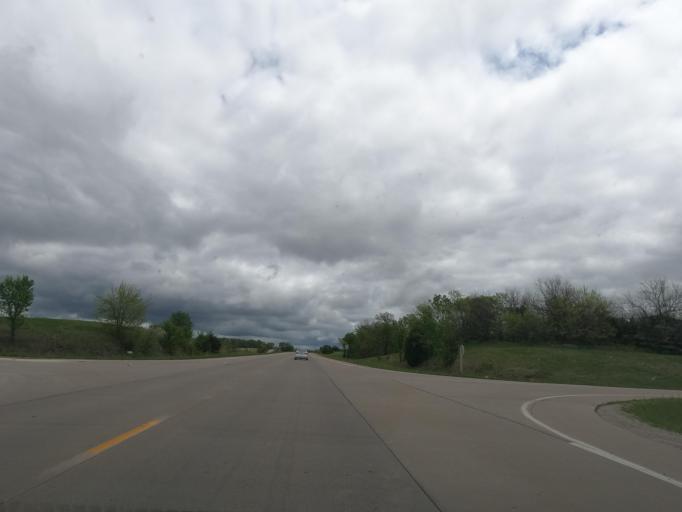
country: US
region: Kansas
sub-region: Wilson County
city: Neodesha
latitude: 37.3551
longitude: -95.6567
